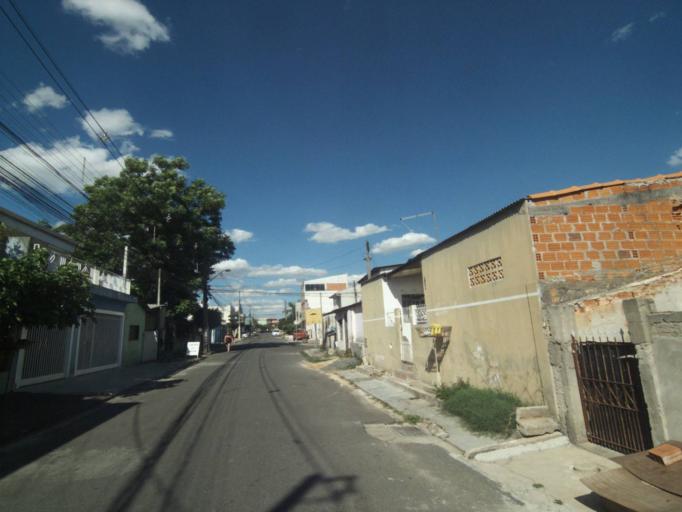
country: BR
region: Parana
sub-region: Curitiba
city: Curitiba
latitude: -25.5125
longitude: -49.3358
